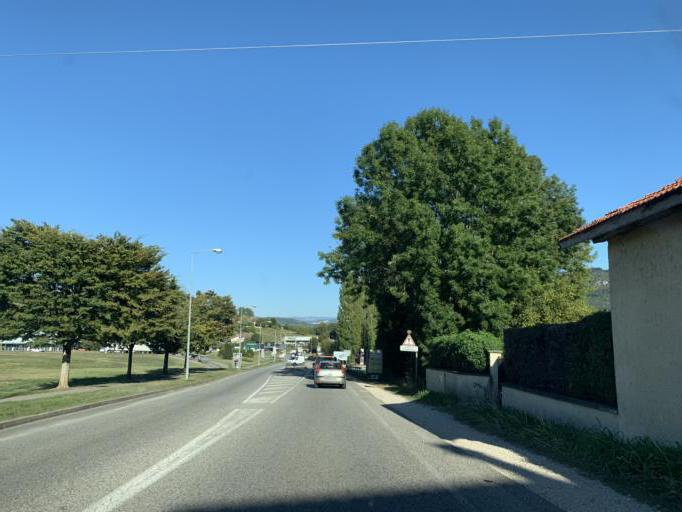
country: FR
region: Rhone-Alpes
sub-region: Departement de l'Ain
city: Belley
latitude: 45.7576
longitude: 5.7020
